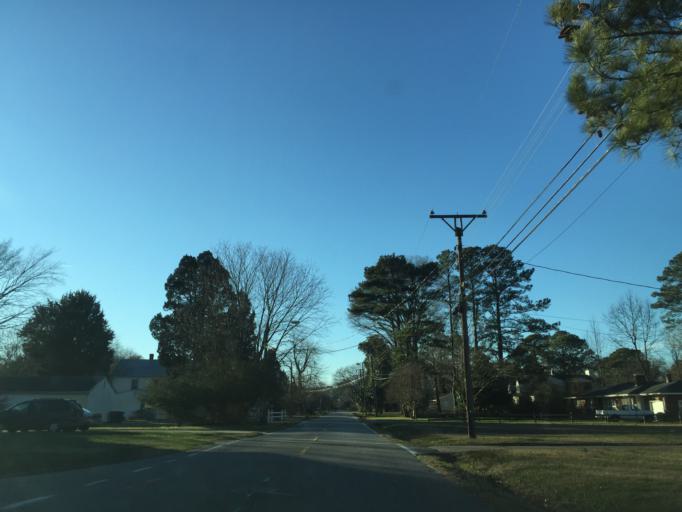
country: US
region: Virginia
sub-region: City of Newport News
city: Newport News
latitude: 37.0777
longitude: -76.5171
